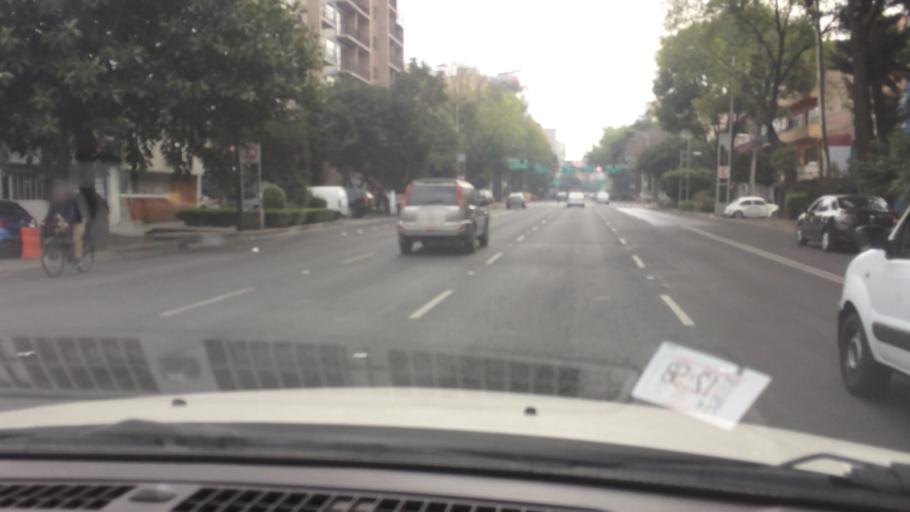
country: MX
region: Mexico City
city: Colonia del Valle
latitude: 19.3905
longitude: -99.1565
